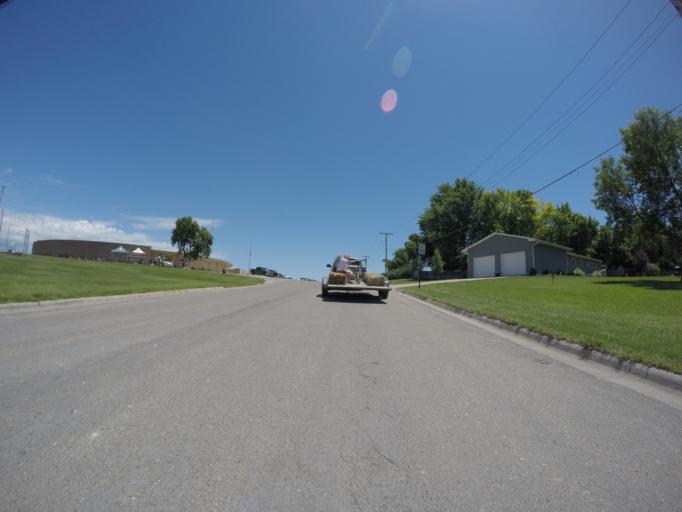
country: US
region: Kansas
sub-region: Jewell County
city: Mankato
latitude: 39.7882
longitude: -98.2029
